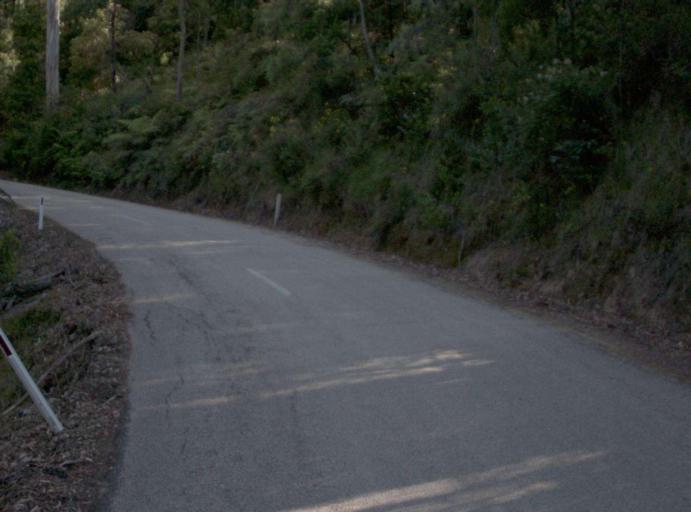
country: AU
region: Victoria
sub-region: East Gippsland
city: Lakes Entrance
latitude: -37.4279
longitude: 148.6028
